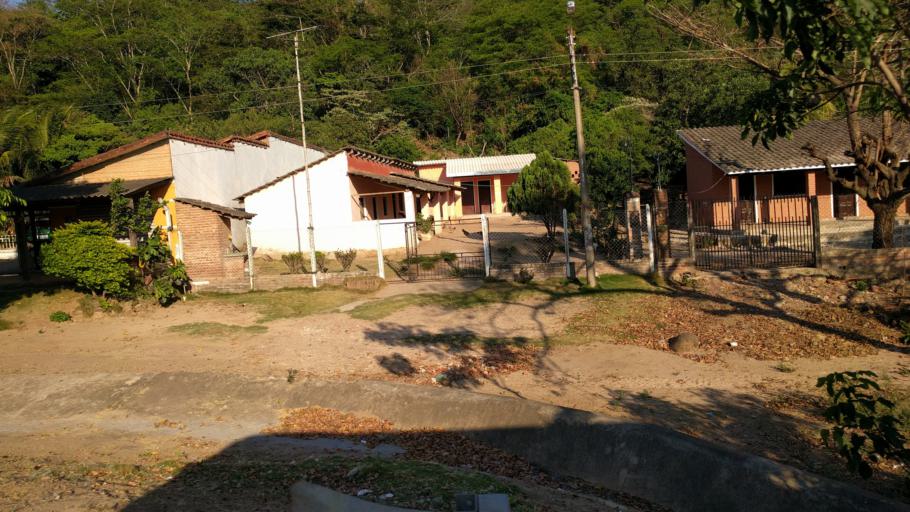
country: BO
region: Santa Cruz
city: Limoncito
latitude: -18.0292
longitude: -63.4028
